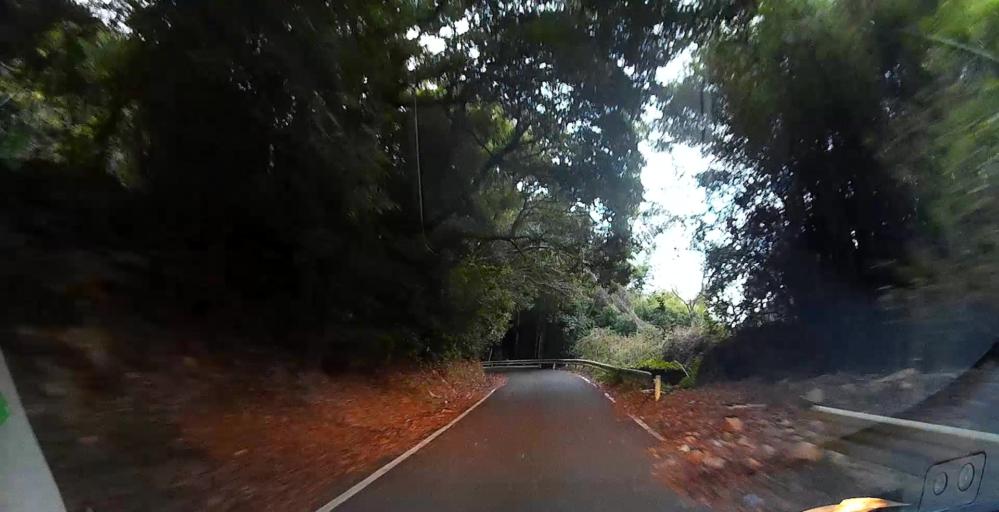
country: JP
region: Kagoshima
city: Izumi
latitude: 32.0970
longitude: 130.3978
